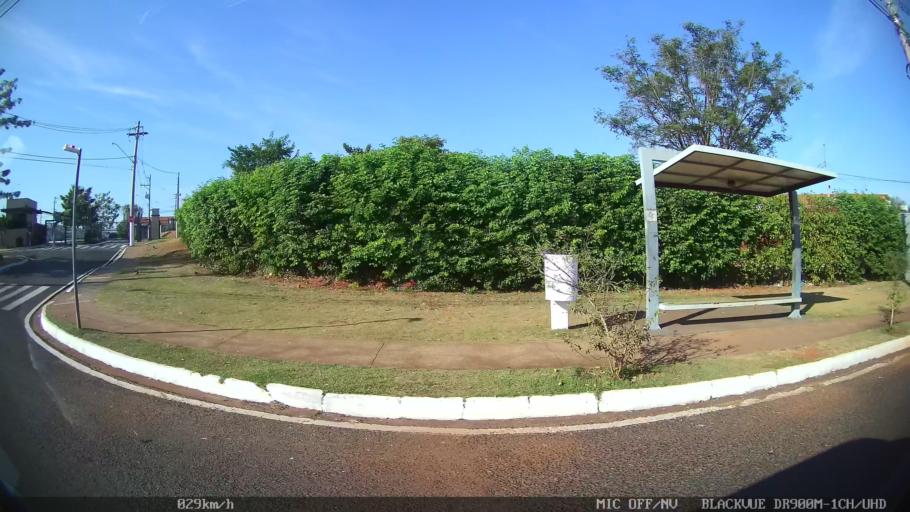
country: BR
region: Sao Paulo
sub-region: Sao Jose Do Rio Preto
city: Sao Jose do Rio Preto
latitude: -20.7703
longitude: -49.3294
